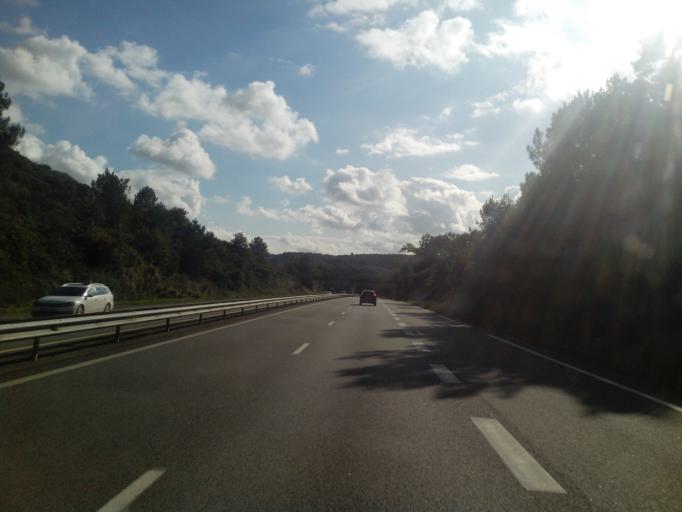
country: FR
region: Brittany
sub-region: Departement du Morbihan
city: Serent
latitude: 47.7978
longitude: -2.4492
